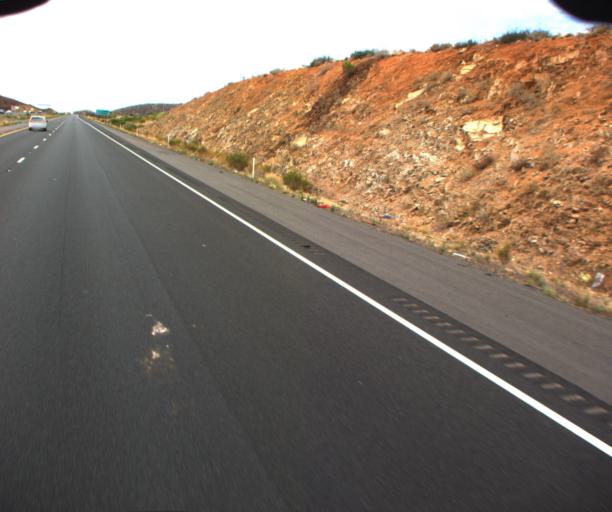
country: US
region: Arizona
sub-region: Yavapai County
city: Cordes Lakes
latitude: 34.3192
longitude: -112.1236
